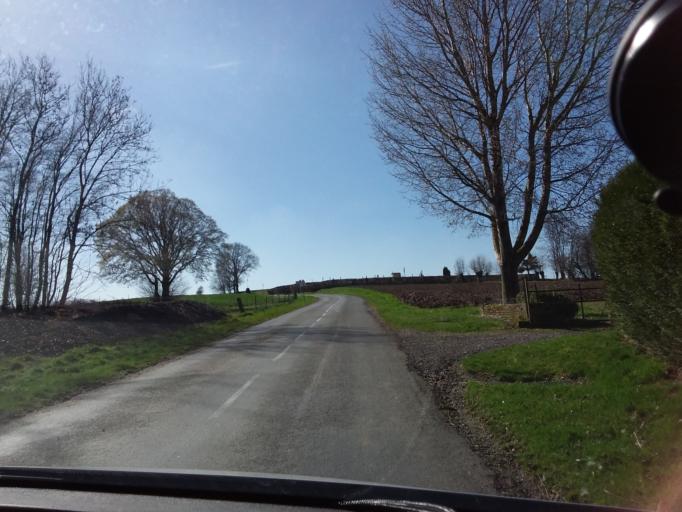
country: FR
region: Picardie
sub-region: Departement de l'Aisne
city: Montcornet
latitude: 49.7763
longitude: 4.0052
